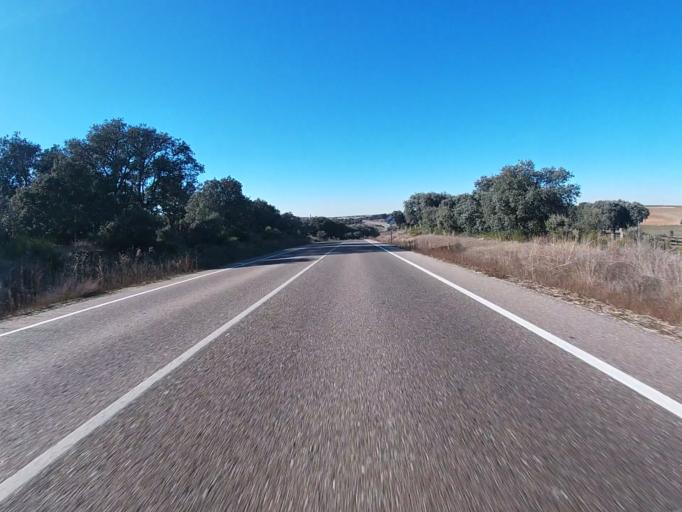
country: ES
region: Castille and Leon
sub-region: Provincia de Salamanca
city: Juzbado
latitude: 41.0766
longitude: -5.8406
